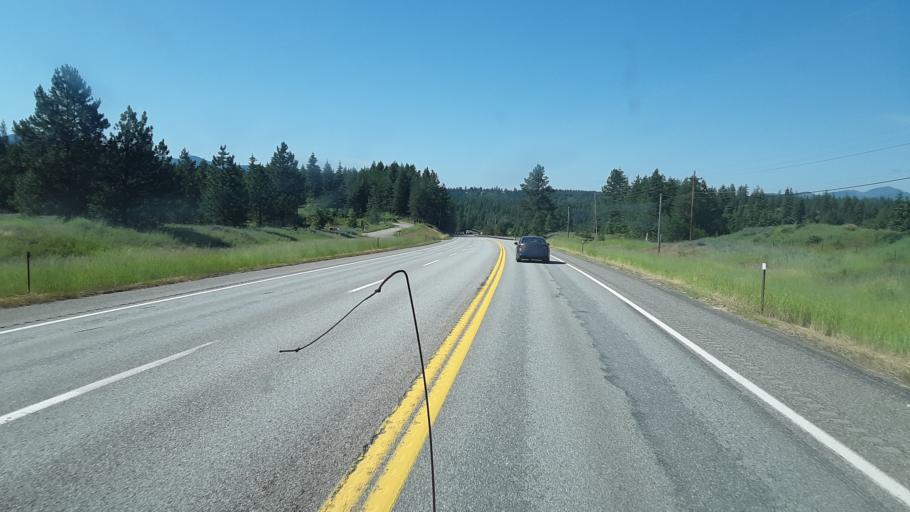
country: US
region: Idaho
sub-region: Kootenai County
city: Spirit Lake
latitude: 48.0012
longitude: -116.6743
